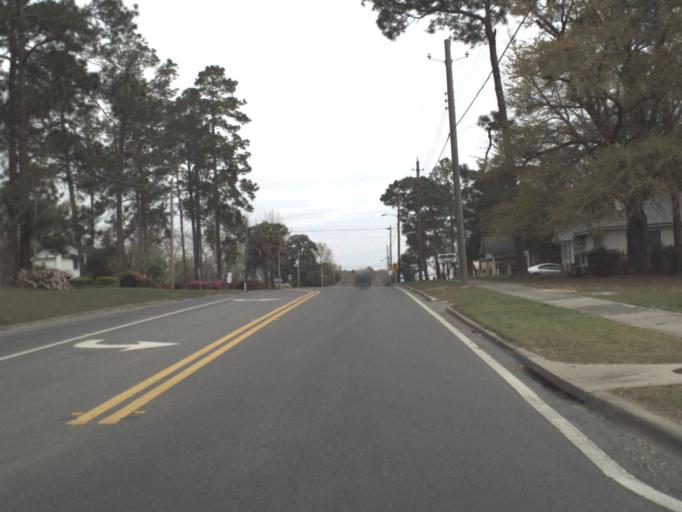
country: US
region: Florida
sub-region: Holmes County
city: Bonifay
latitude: 30.7972
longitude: -85.6795
